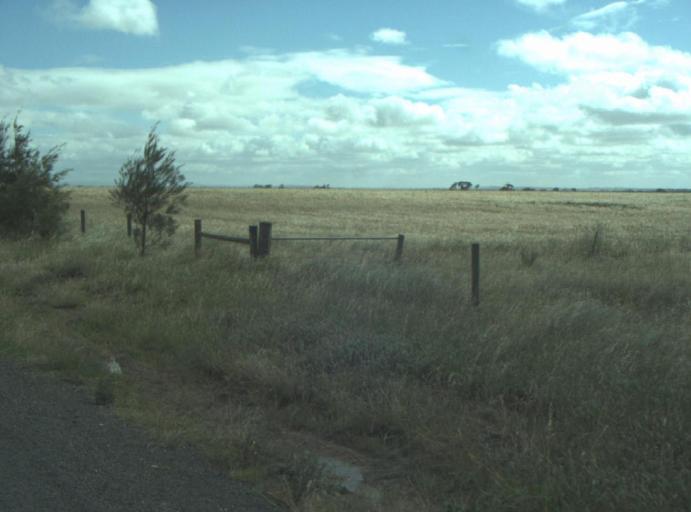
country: AU
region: Victoria
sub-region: Greater Geelong
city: Lara
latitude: -37.8914
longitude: 144.3193
